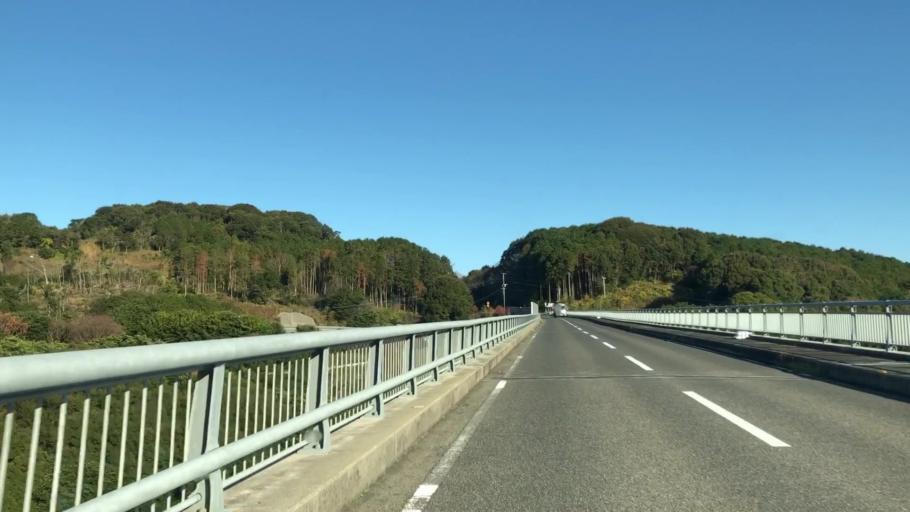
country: JP
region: Nagasaki
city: Sasebo
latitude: 33.0057
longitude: 129.7074
